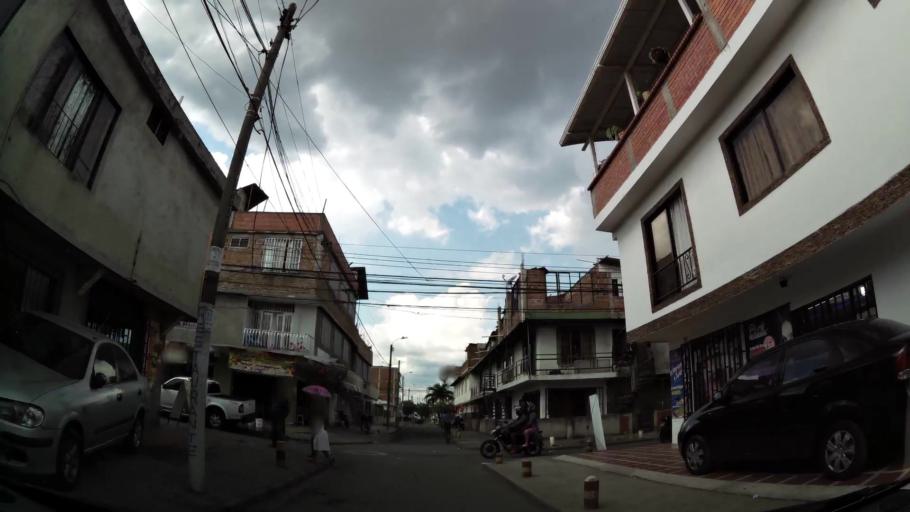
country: CO
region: Valle del Cauca
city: Cali
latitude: 3.4857
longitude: -76.5001
